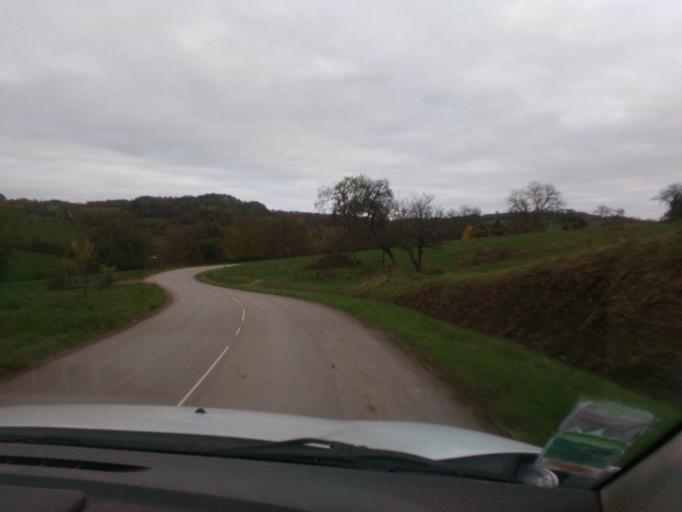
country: FR
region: Lorraine
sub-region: Departement des Vosges
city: Darnieulles
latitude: 48.2560
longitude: 6.2789
